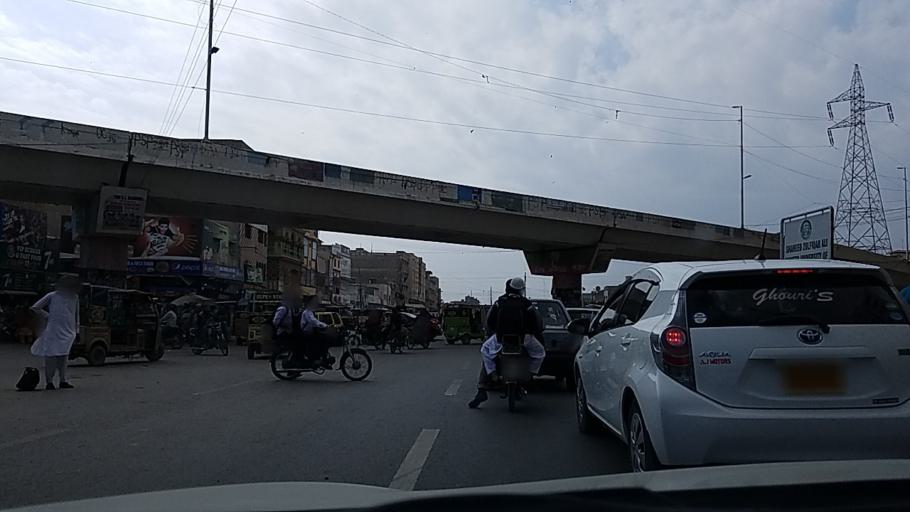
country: PK
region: Sindh
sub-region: Karachi District
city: Karachi
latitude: 24.8171
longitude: 67.1084
